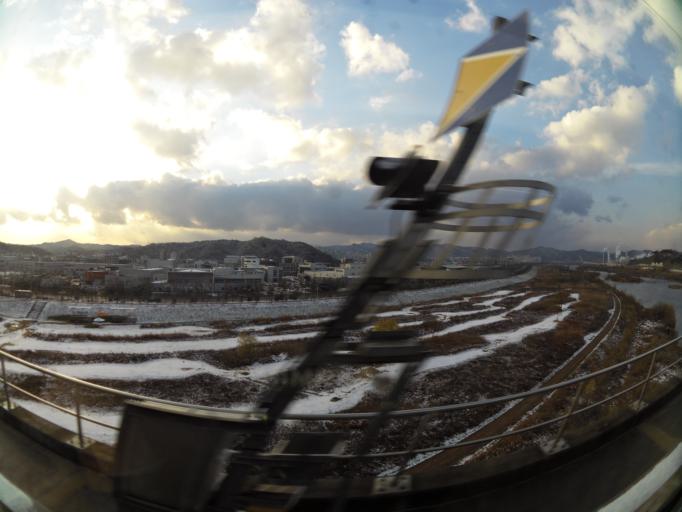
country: KR
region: Daejeon
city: Songgang-dong
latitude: 36.4189
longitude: 127.4157
